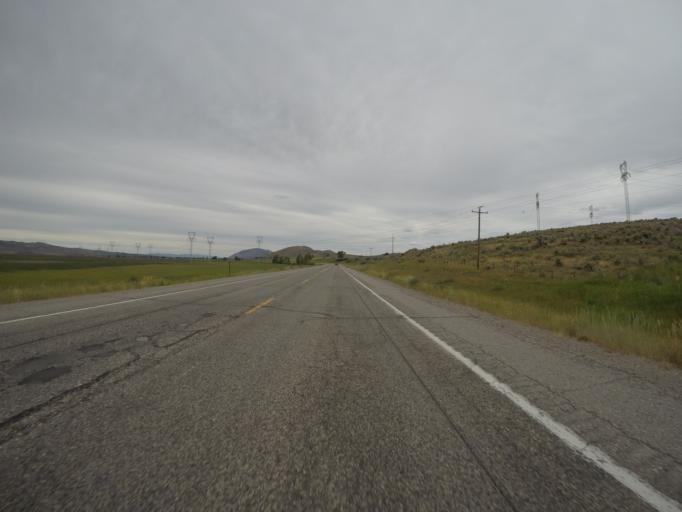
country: US
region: Idaho
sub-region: Bear Lake County
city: Montpelier
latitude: 42.0534
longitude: -110.9313
